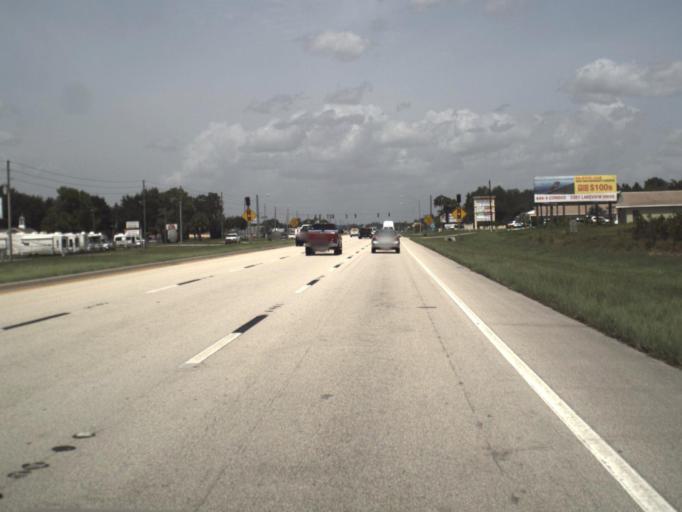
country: US
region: Florida
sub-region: Highlands County
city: Sebring
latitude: 27.4391
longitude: -81.4188
